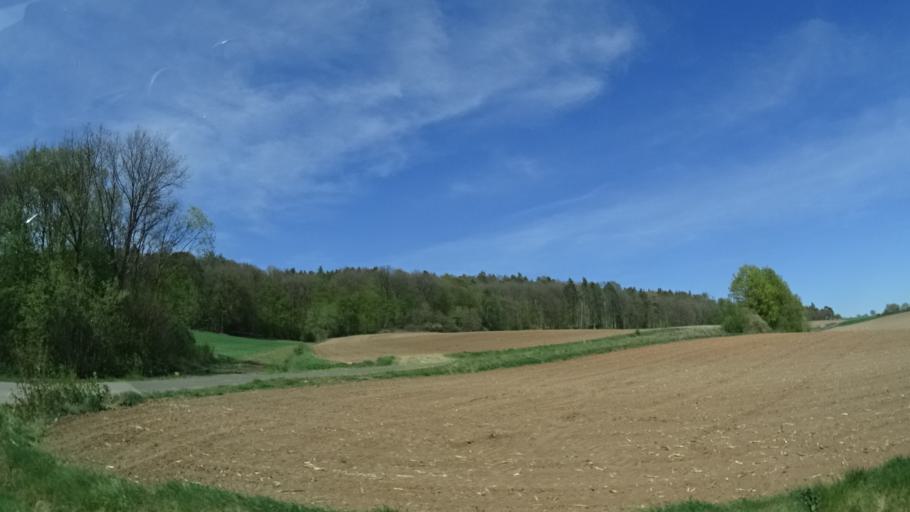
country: DE
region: Bavaria
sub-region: Regierungsbezirk Unterfranken
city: Burgpreppach
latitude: 50.1549
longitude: 10.6191
